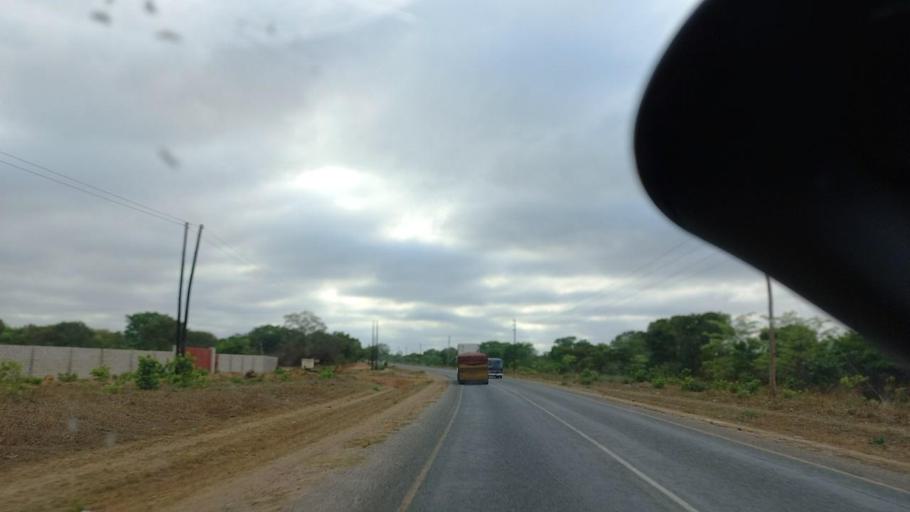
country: ZM
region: Lusaka
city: Chongwe
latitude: -15.3519
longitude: 28.5404
